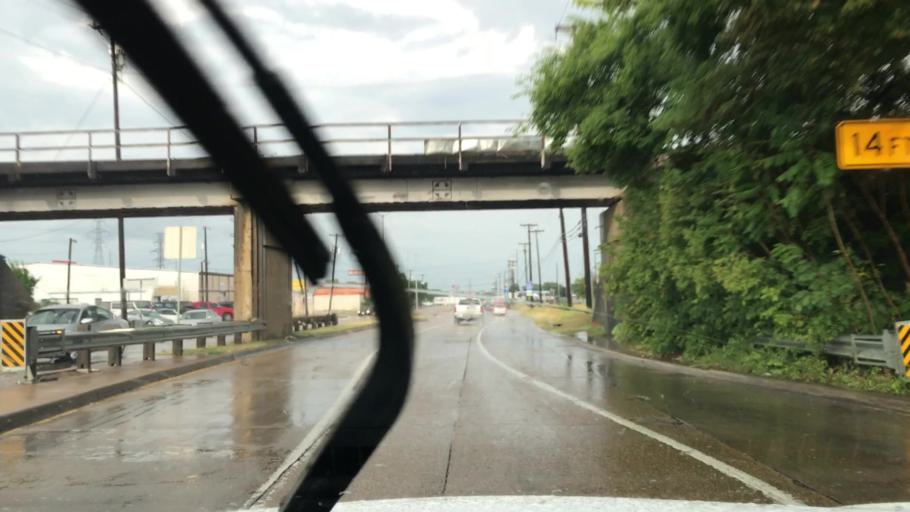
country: US
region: Texas
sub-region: Dallas County
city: Garland
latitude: 32.8641
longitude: -96.6701
